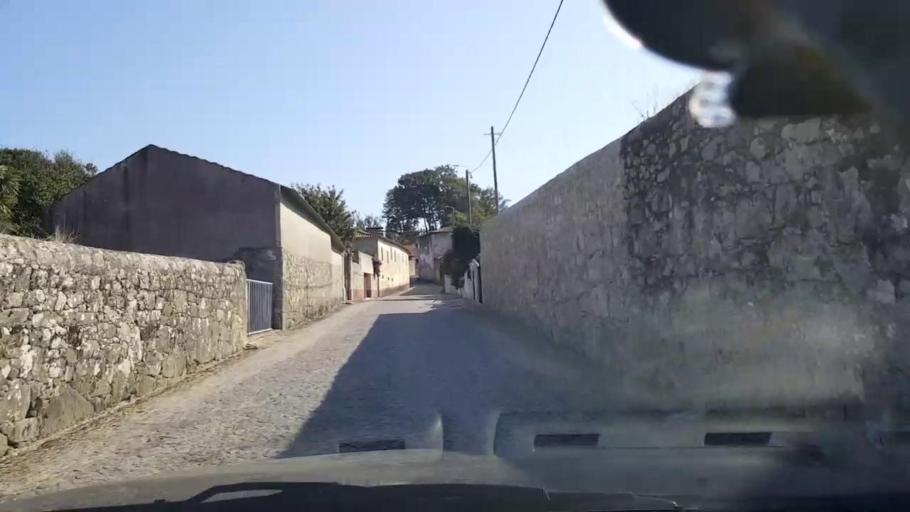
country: PT
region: Porto
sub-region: Vila do Conde
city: Arvore
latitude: 41.3631
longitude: -8.7018
